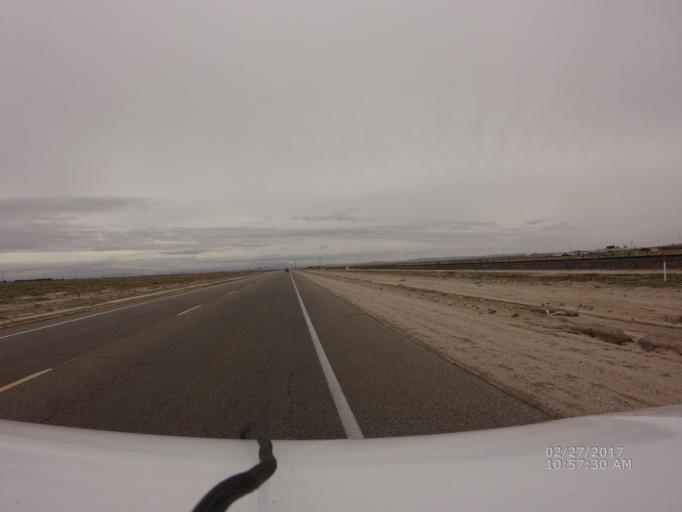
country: US
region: California
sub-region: Los Angeles County
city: Lancaster
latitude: 34.7454
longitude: -118.1441
